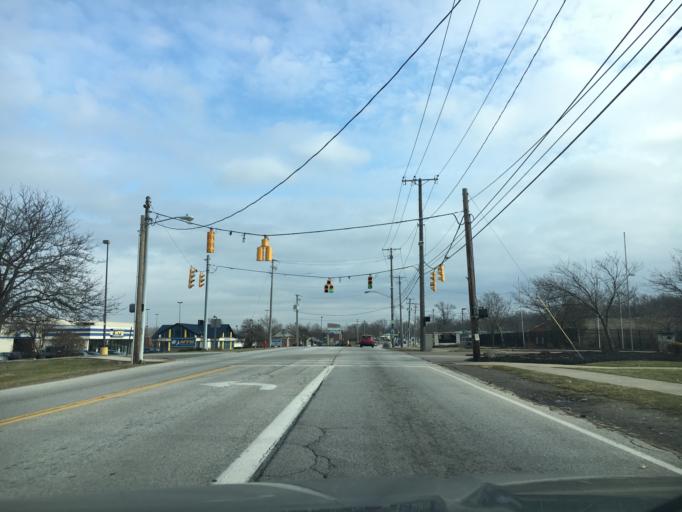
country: US
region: Ohio
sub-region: Cuyahoga County
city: Highland Heights
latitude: 41.5825
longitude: -81.4867
